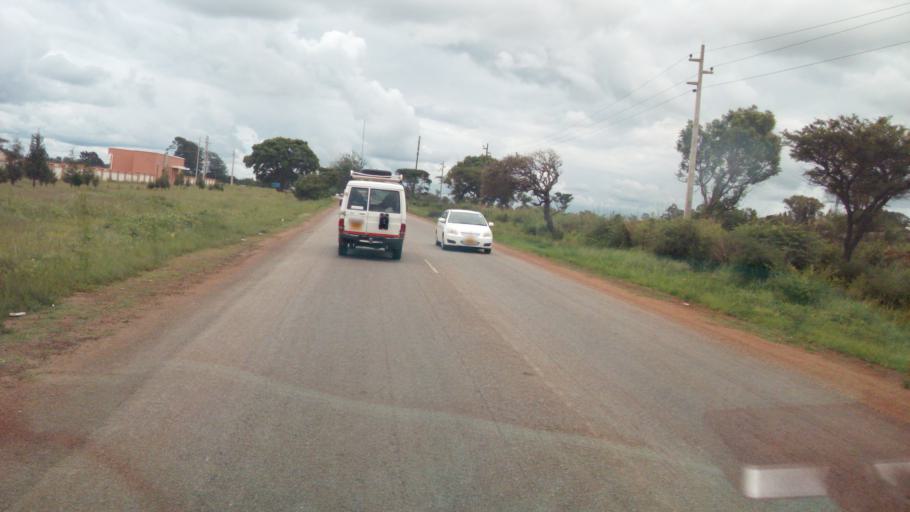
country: ZW
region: Harare
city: Harare
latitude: -17.7298
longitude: 31.0223
